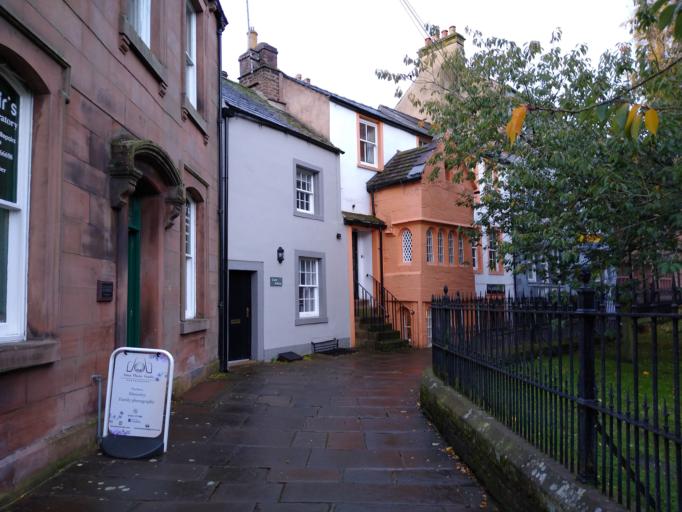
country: GB
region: England
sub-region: Cumbria
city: Penrith
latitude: 54.6638
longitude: -2.7514
